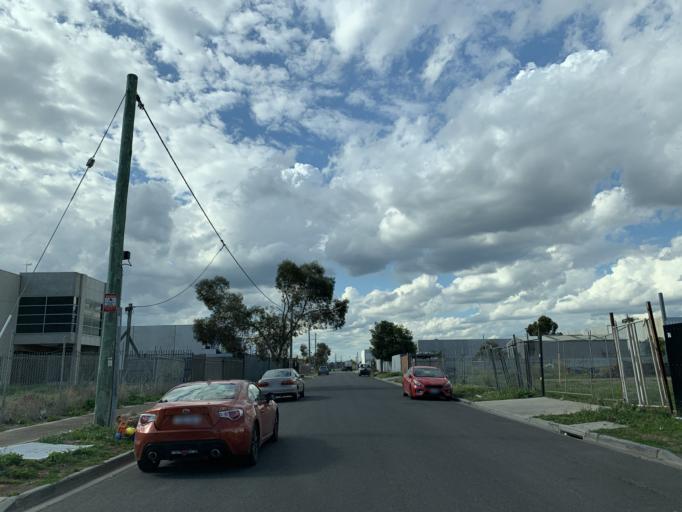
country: AU
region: Victoria
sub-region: Brimbank
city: Albion
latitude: -37.7531
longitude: 144.8394
